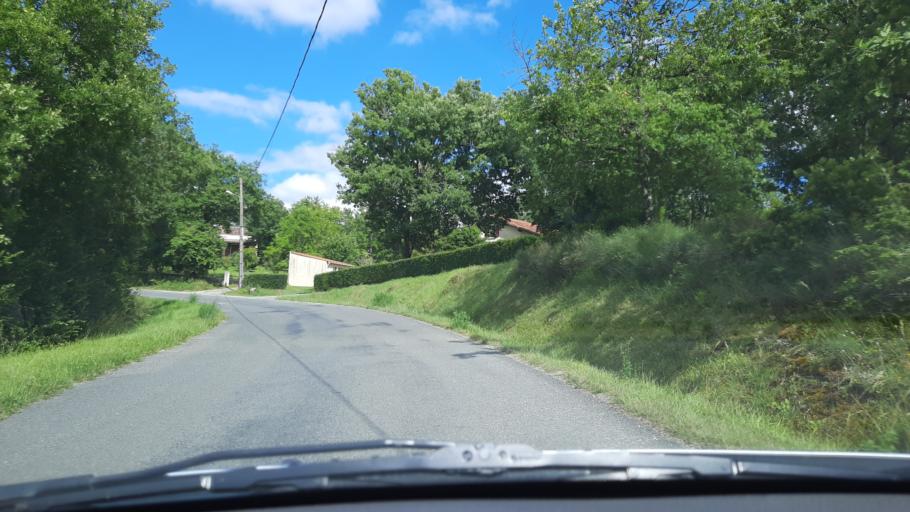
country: FR
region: Midi-Pyrenees
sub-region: Departement du Lot
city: Castelnau-Montratier
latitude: 44.2942
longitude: 1.4537
